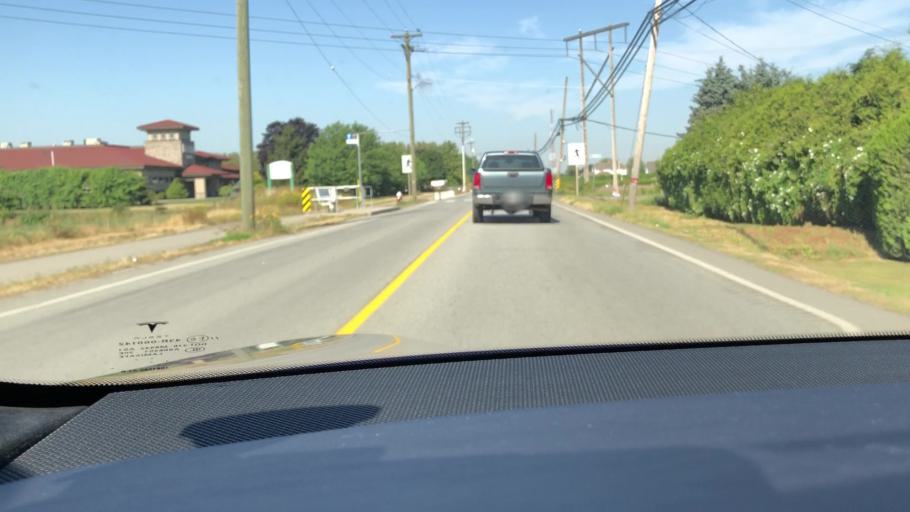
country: CA
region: British Columbia
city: Ladner
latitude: 49.1696
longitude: -123.0345
